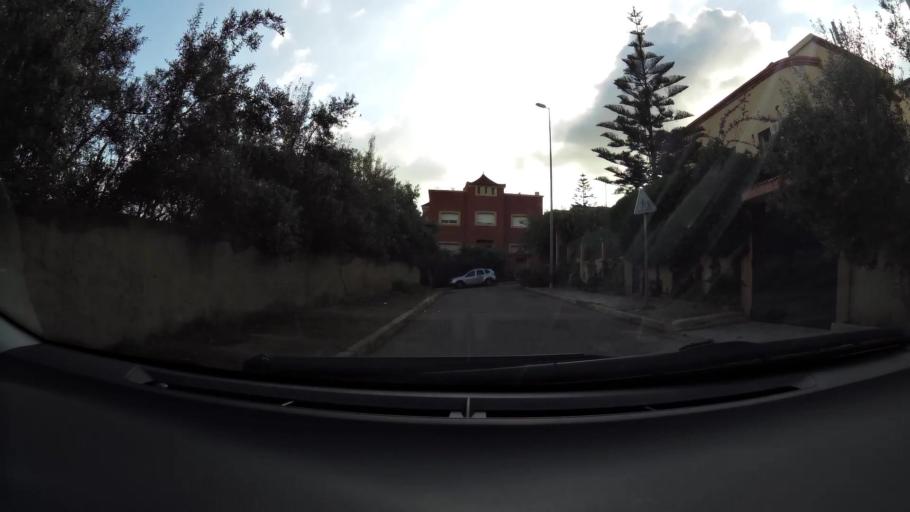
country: MA
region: Chaouia-Ouardigha
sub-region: Settat Province
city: Settat
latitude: 33.0105
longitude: -7.6328
